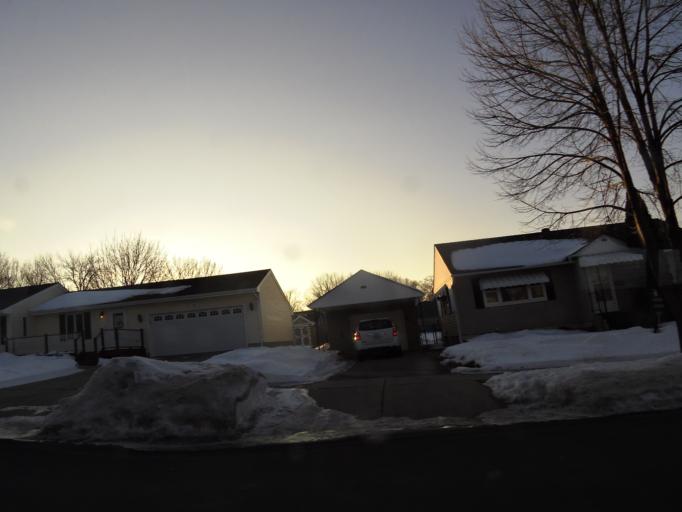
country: US
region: Minnesota
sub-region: Scott County
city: Shakopee
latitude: 44.7909
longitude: -93.5204
